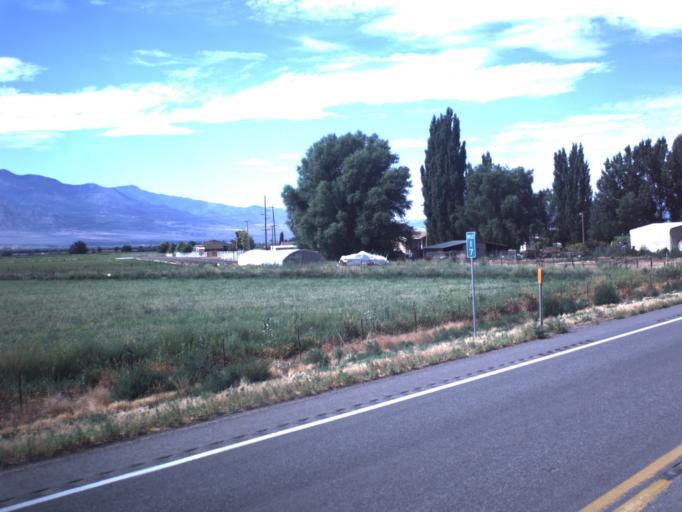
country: US
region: Utah
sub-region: Sevier County
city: Richfield
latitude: 38.7879
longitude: -112.0499
